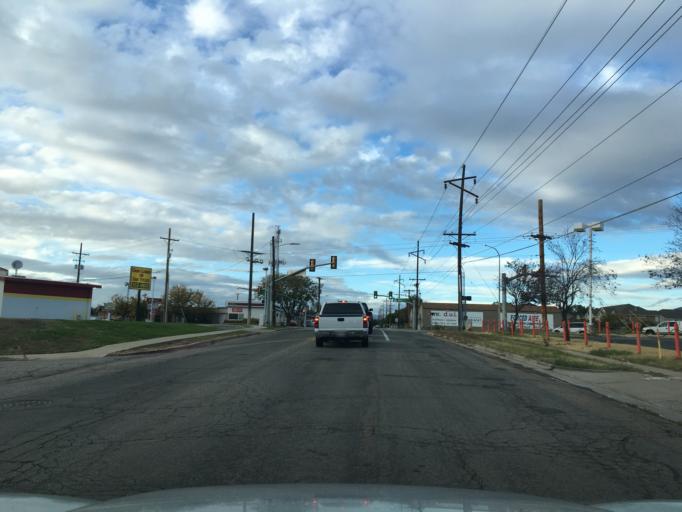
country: US
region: Utah
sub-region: Davis County
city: Layton
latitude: 41.0786
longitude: -111.9878
